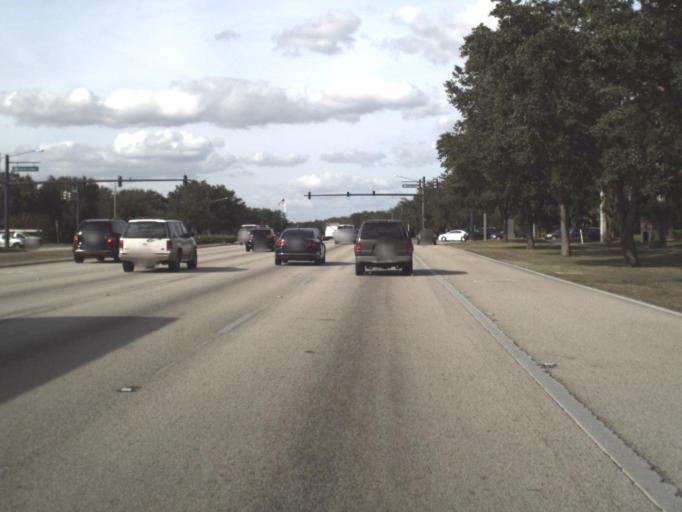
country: US
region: Florida
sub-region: Orange County
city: Hunters Creek
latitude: 28.3520
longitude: -81.4195
